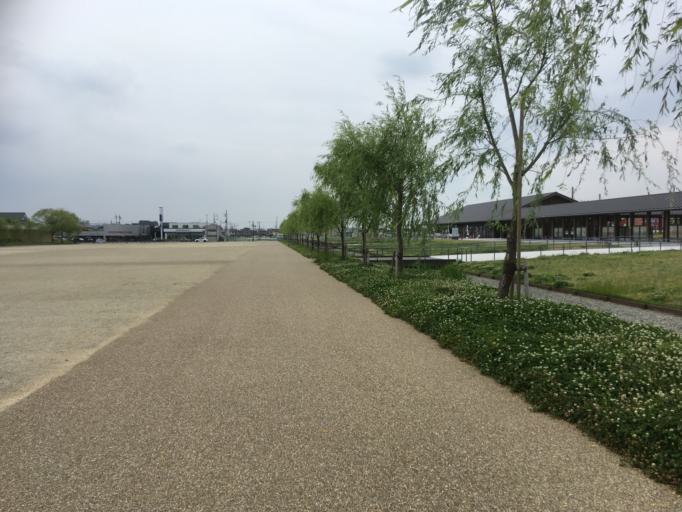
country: JP
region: Nara
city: Nara-shi
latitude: 34.6863
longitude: 135.7940
